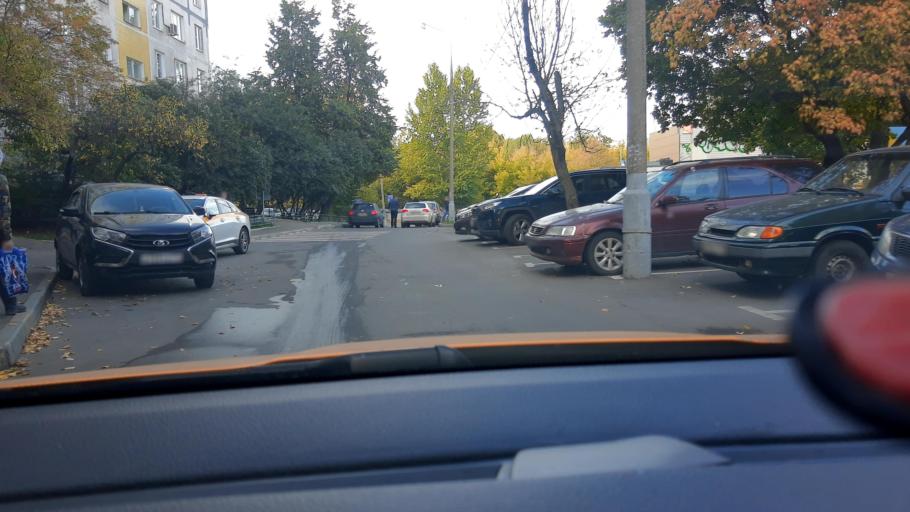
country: RU
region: Moscow
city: Orekhovo-Borisovo
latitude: 55.6100
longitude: 37.7399
